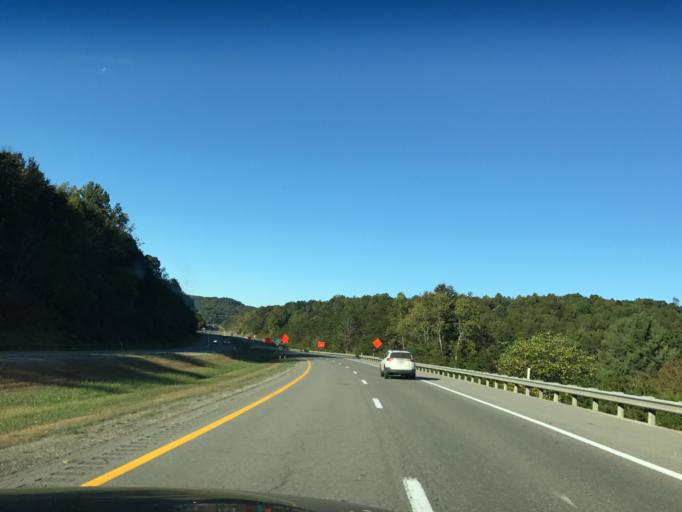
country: US
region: Ohio
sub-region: Washington County
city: Reno
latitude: 39.2531
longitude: -81.3444
